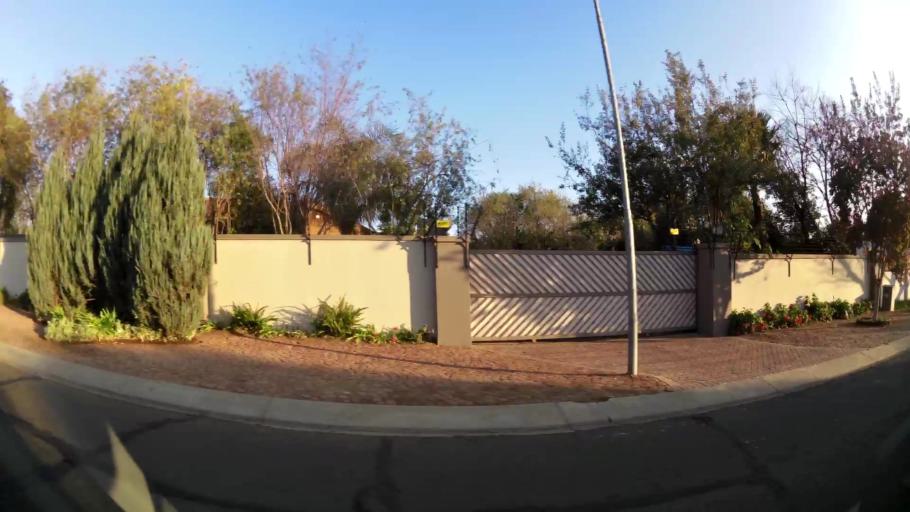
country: ZA
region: Orange Free State
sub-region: Mangaung Metropolitan Municipality
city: Bloemfontein
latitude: -29.0886
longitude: 26.1556
